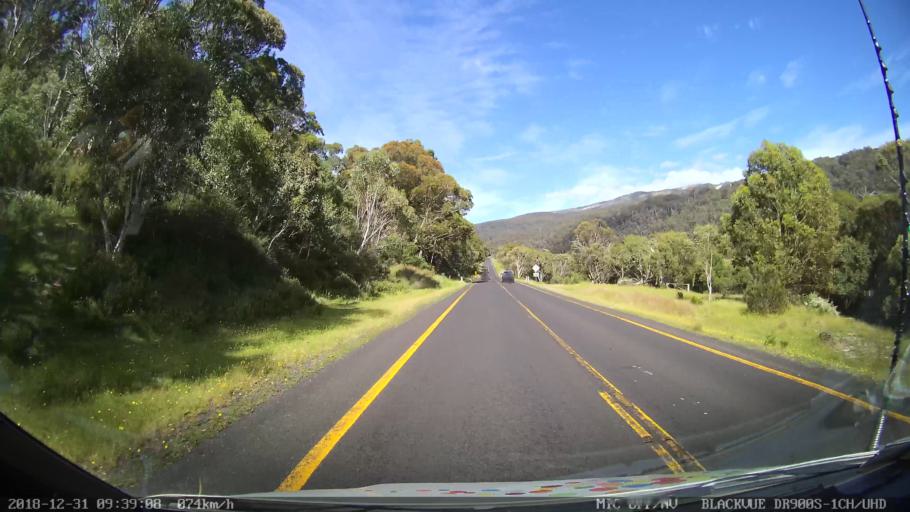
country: AU
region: New South Wales
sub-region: Snowy River
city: Jindabyne
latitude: -36.4781
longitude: 148.3592
